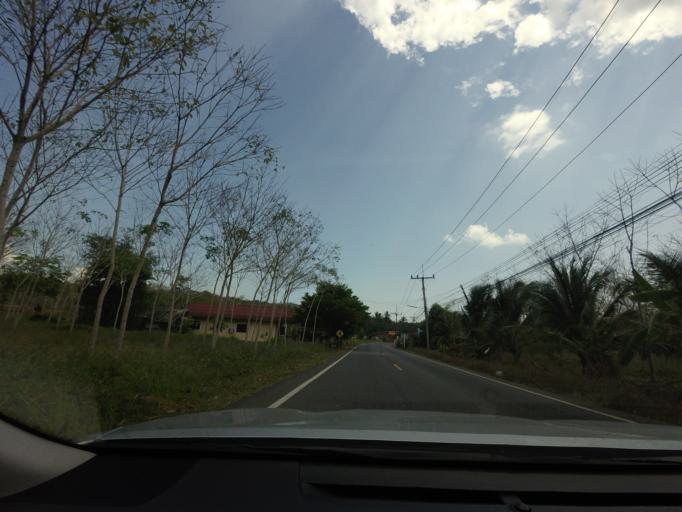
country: TH
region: Phangnga
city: Takua Thung
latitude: 8.2521
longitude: 98.3850
